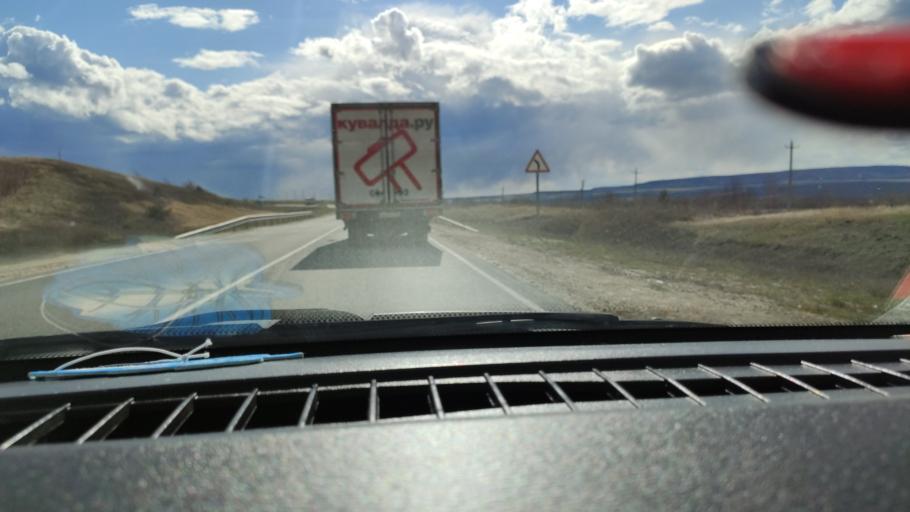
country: RU
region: Saratov
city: Alekseyevka
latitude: 52.3312
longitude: 47.9223
